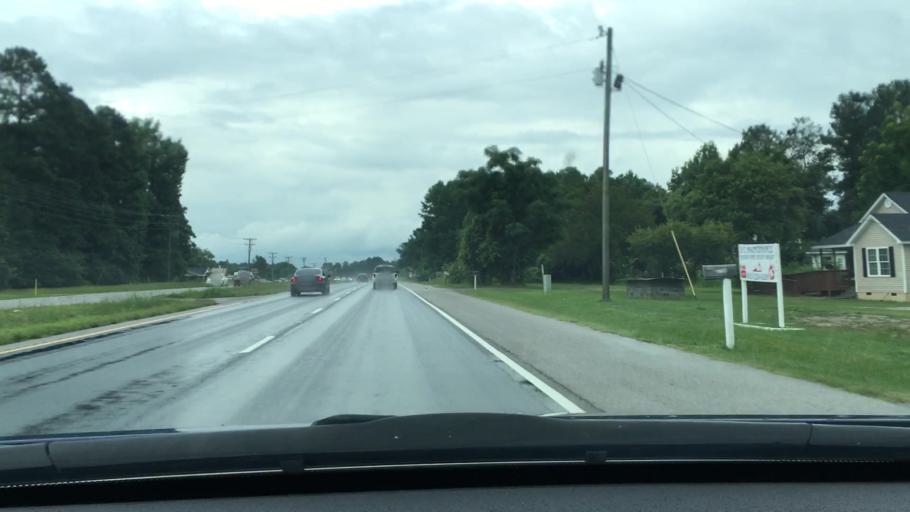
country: US
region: South Carolina
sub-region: Sumter County
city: Cherryvale
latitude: 33.9643
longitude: -80.4368
